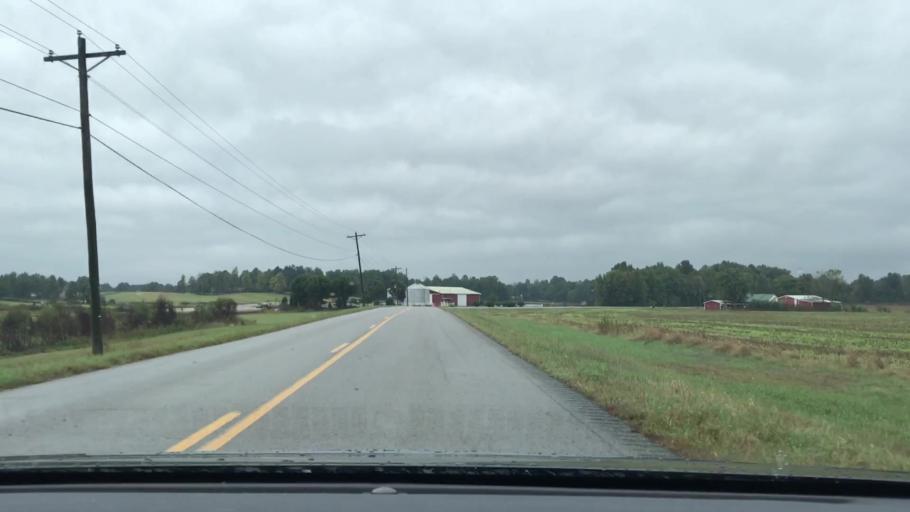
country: US
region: Kentucky
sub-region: McLean County
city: Calhoun
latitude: 37.4550
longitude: -87.2350
